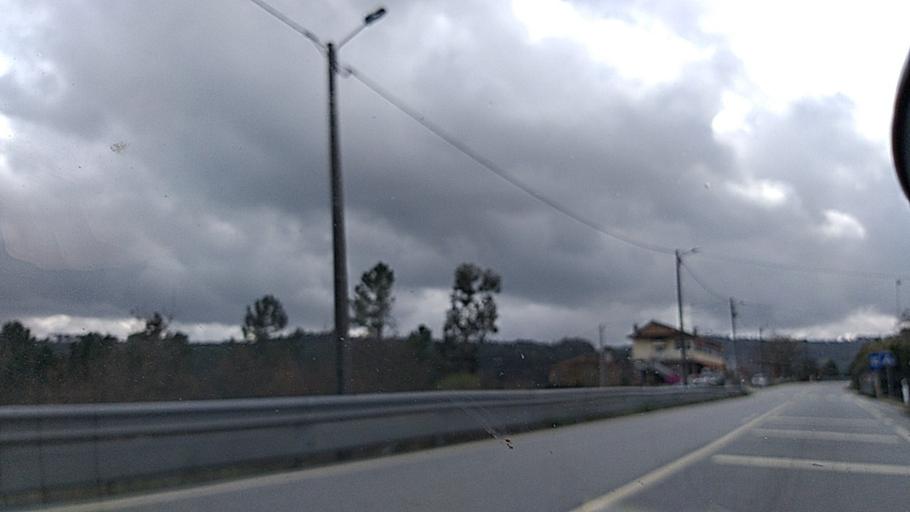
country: PT
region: Viseu
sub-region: Mangualde
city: Mangualde
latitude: 40.6350
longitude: -7.7395
